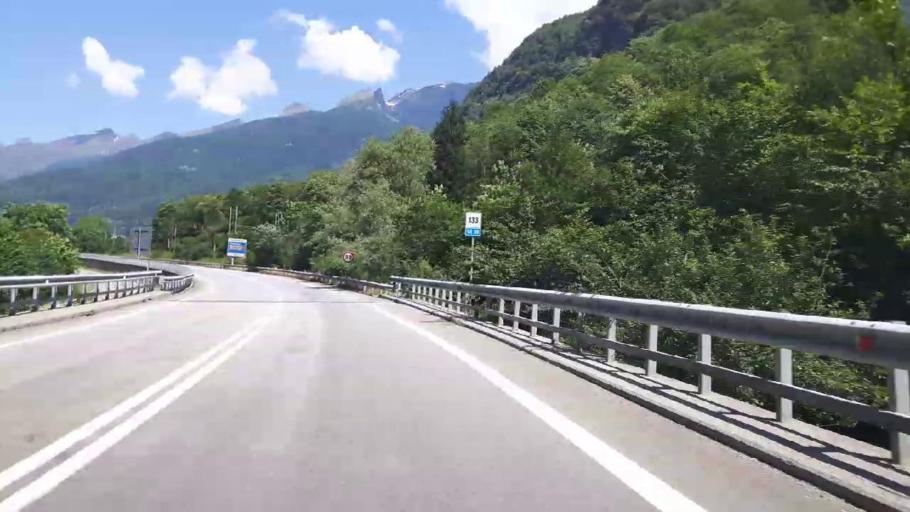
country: IT
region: Piedmont
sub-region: Provincia Verbano-Cusio-Ossola
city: Varzo
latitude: 46.1889
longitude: 8.2772
